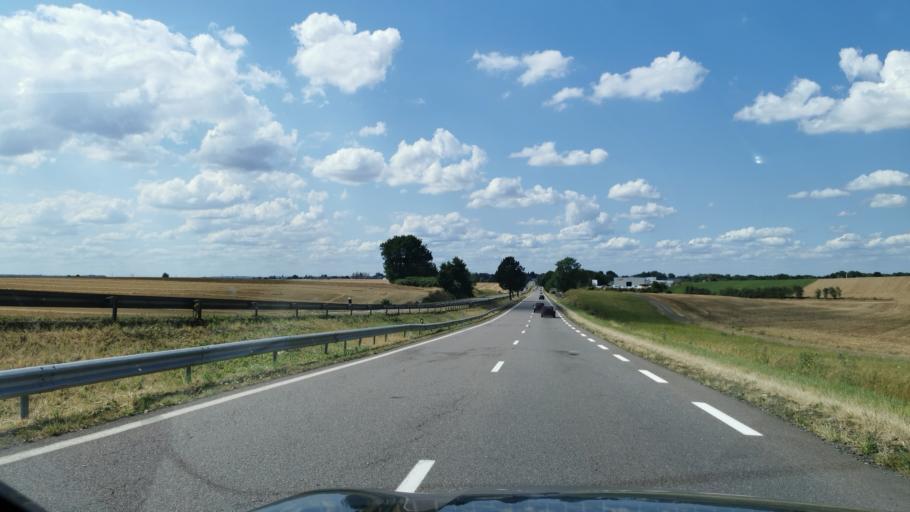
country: FR
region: Lorraine
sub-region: Departement de Meurthe-et-Moselle
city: Villers-la-Montagne
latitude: 49.4644
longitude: 5.8488
